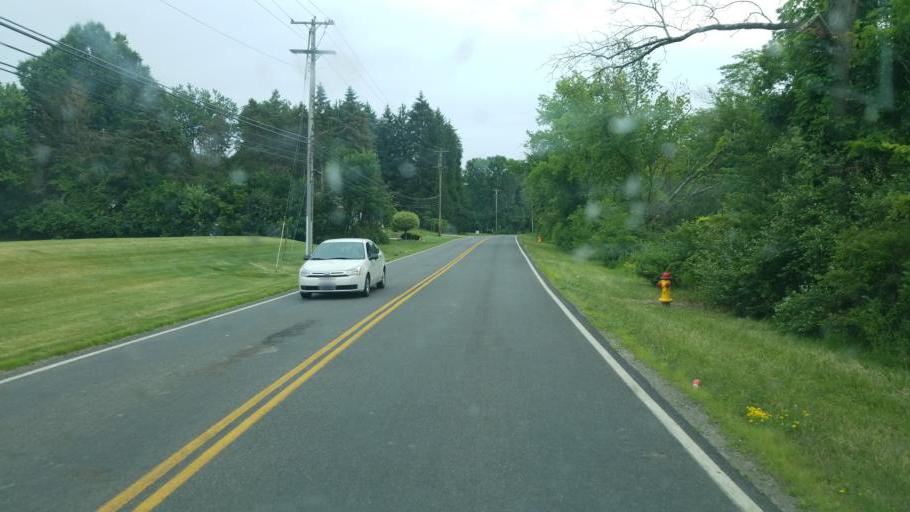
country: US
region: Ohio
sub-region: Stark County
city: Canal Fulton
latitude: 40.8982
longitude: -81.6024
